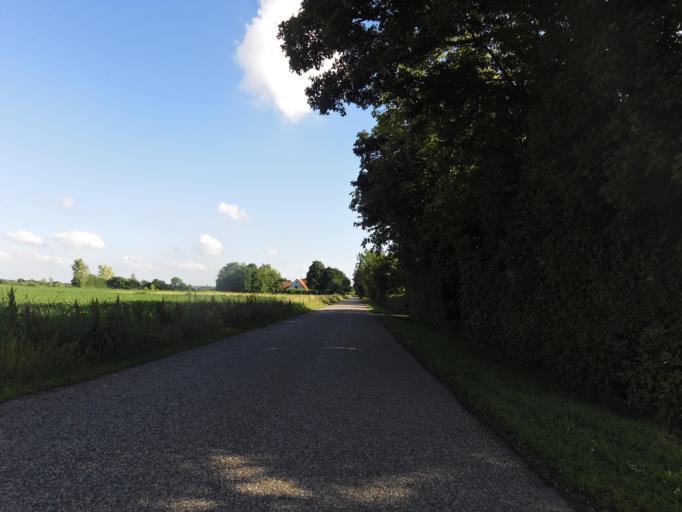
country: DK
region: South Denmark
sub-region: Vejen Kommune
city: Rodding
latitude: 55.3191
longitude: 9.1811
